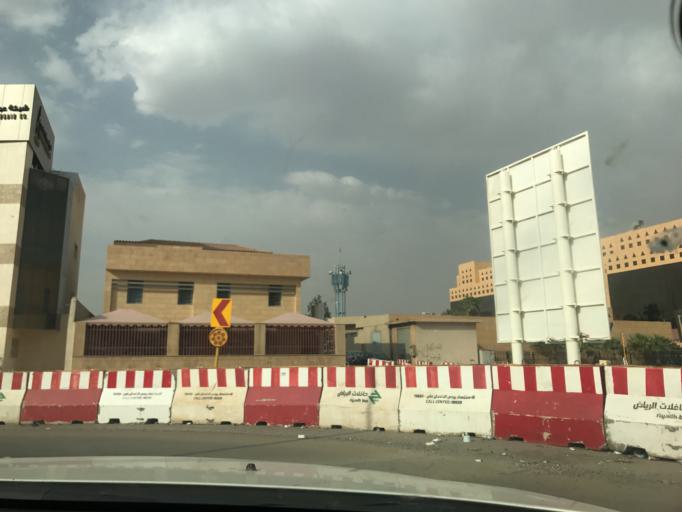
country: SA
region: Ar Riyad
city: Riyadh
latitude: 24.7079
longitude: 46.7124
